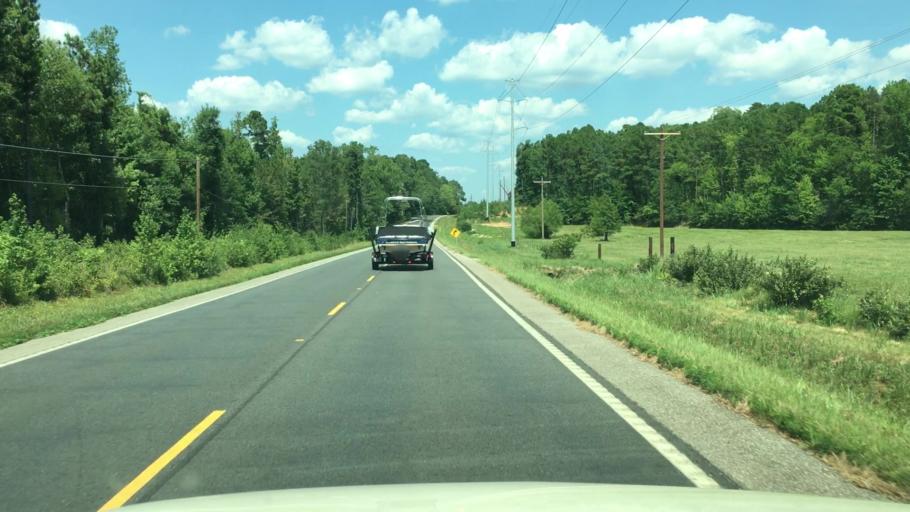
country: US
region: Arkansas
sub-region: Garland County
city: Lake Hamilton
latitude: 34.3991
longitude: -93.1007
